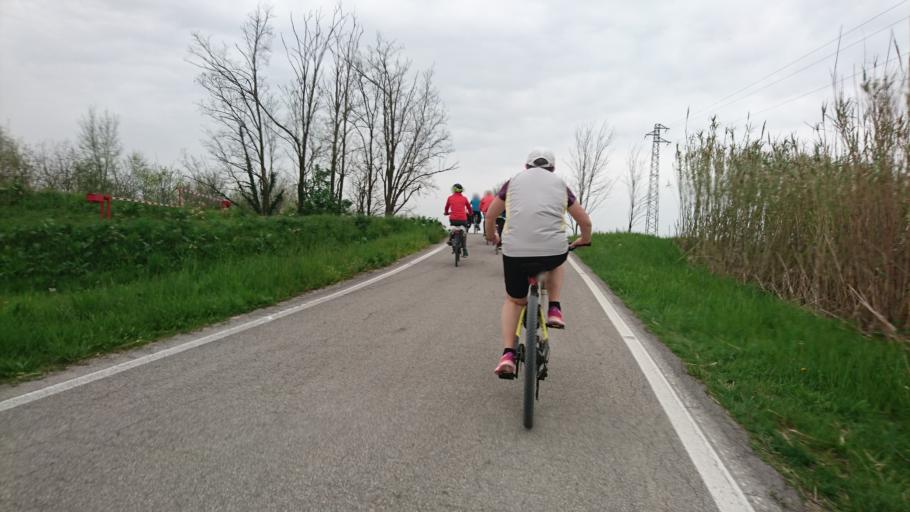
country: IT
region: Veneto
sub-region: Provincia di Venezia
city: Cesarolo
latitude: 45.6873
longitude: 12.9871
